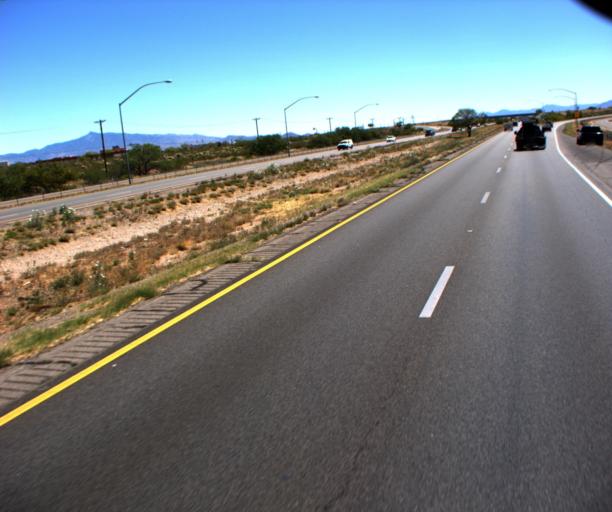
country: US
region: Arizona
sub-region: Pima County
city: Summit
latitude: 32.1083
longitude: -110.8483
